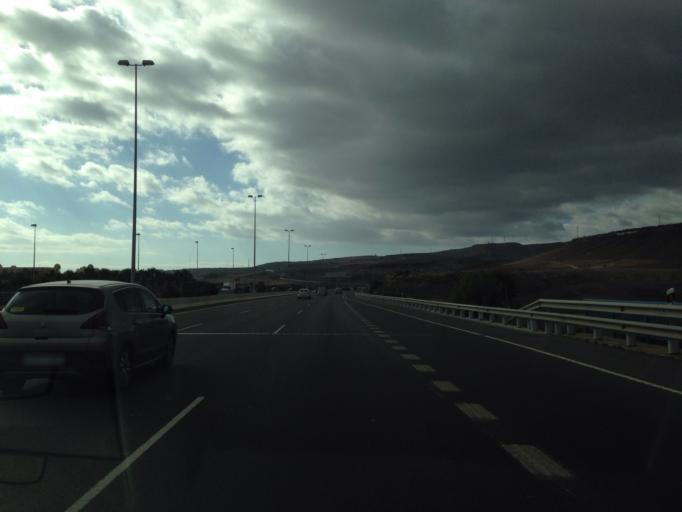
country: ES
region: Canary Islands
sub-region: Provincia de Las Palmas
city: Playa del Ingles
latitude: 27.7877
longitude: -15.5079
